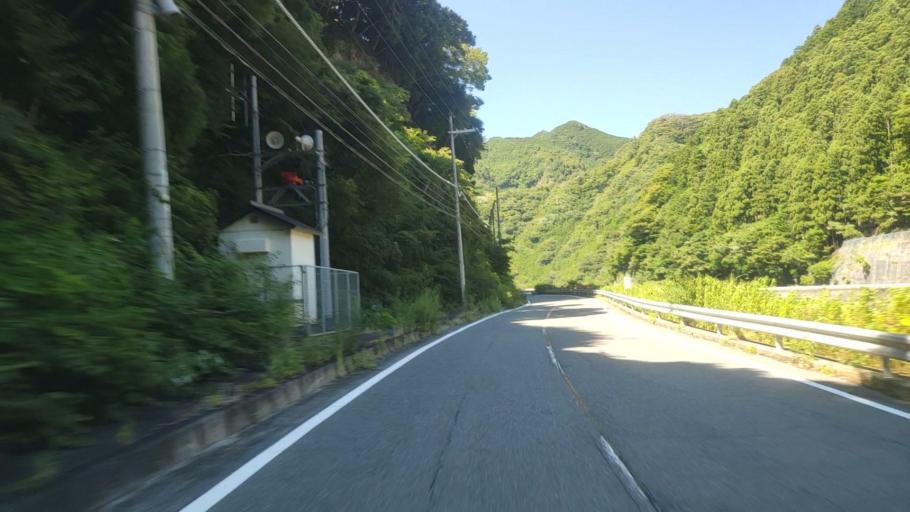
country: JP
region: Nara
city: Yoshino-cho
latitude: 34.3047
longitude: 135.9915
